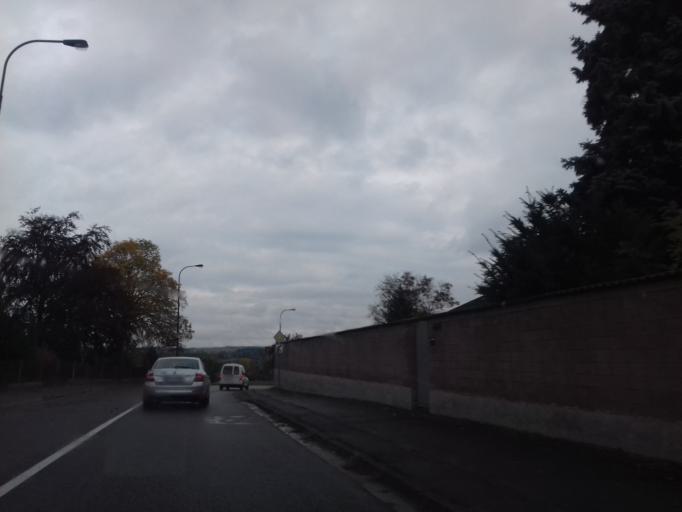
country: CZ
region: Pardubicky
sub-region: Okres Chrudim
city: Chrast
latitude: 49.8988
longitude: 15.9445
